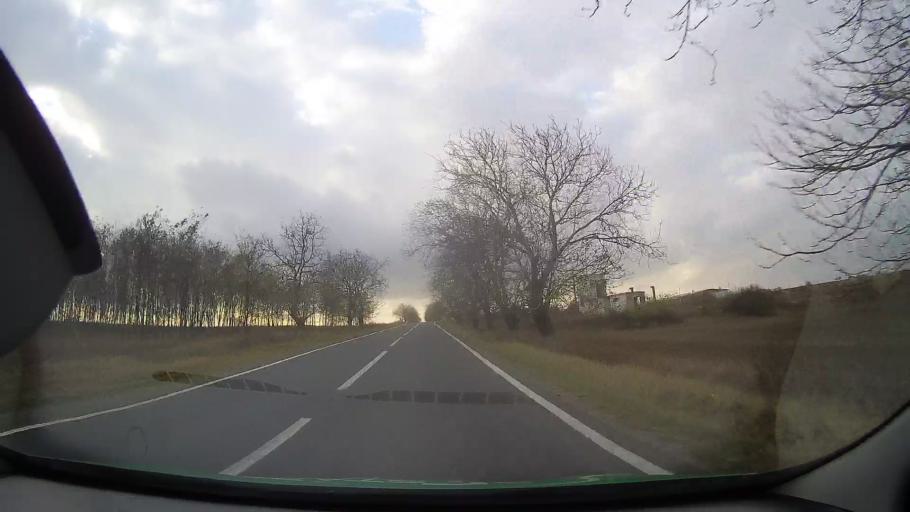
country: RO
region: Constanta
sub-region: Comuna Adamclisi
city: Adamclisi
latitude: 44.0878
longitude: 27.9749
